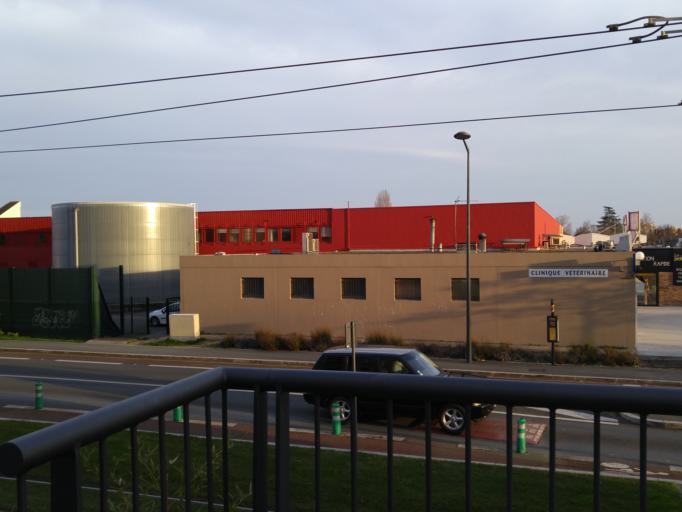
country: FR
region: Pays de la Loire
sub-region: Departement de Maine-et-Loire
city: Angers
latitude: 47.4526
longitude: -0.5561
